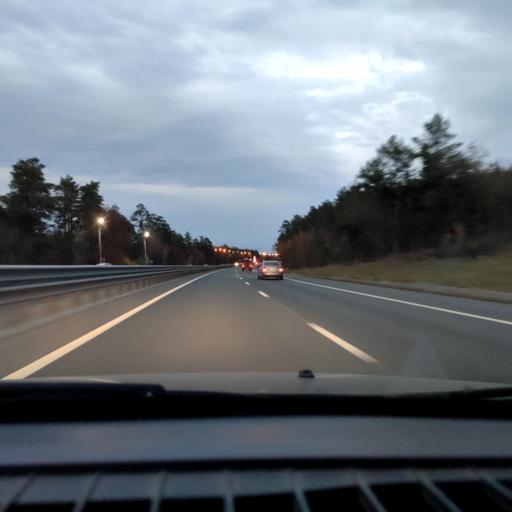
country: RU
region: Samara
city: Zhigulevsk
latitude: 53.5104
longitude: 49.5656
